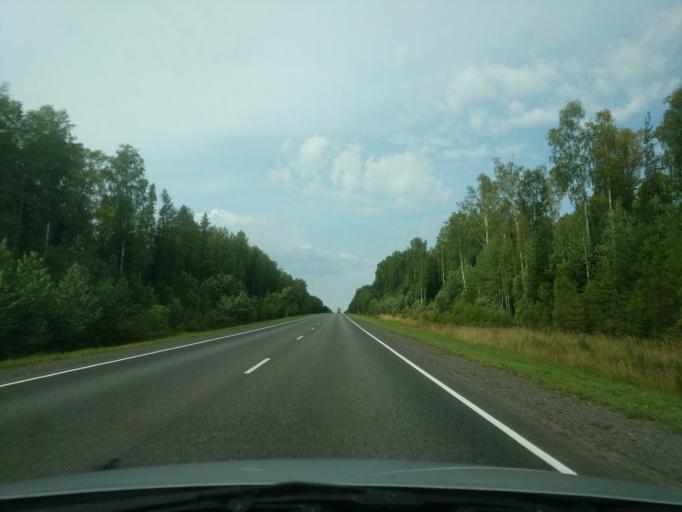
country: RU
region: Kirov
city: Leninskoye
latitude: 58.3187
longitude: 46.8949
